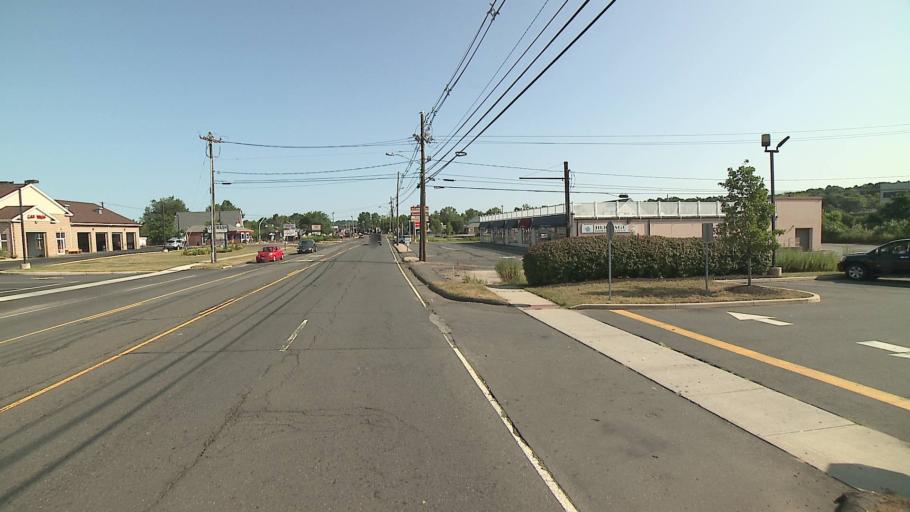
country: US
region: Connecticut
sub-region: New Haven County
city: Wallingford
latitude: 41.4818
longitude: -72.8103
